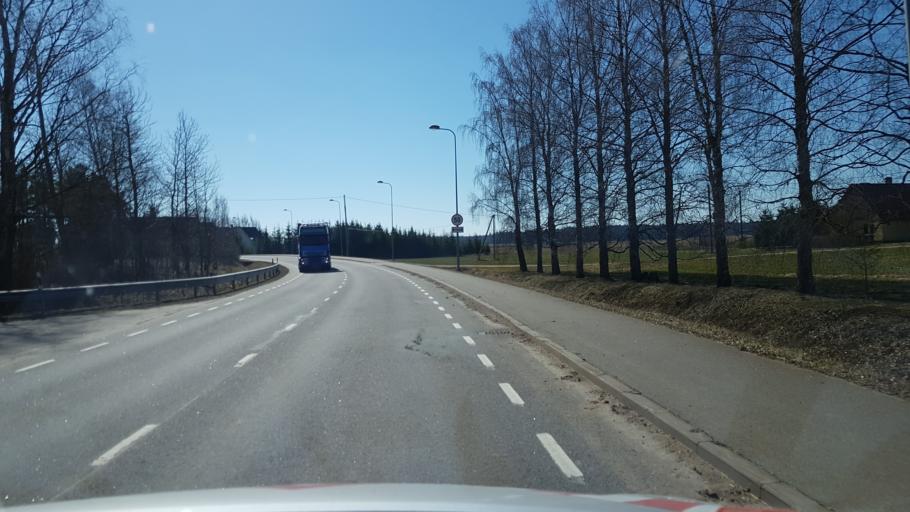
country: EE
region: Laeaene-Virumaa
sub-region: Vinni vald
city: Vinni
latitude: 59.1564
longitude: 26.5882
